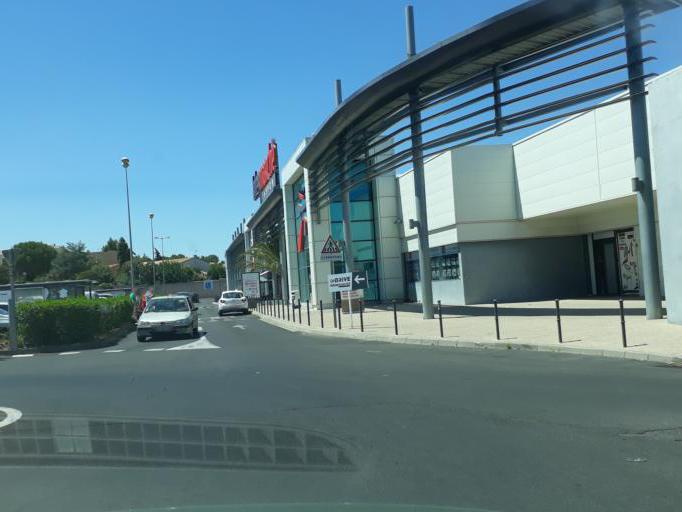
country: FR
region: Languedoc-Roussillon
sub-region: Departement de l'Herault
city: Agde
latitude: 43.3070
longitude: 3.4915
